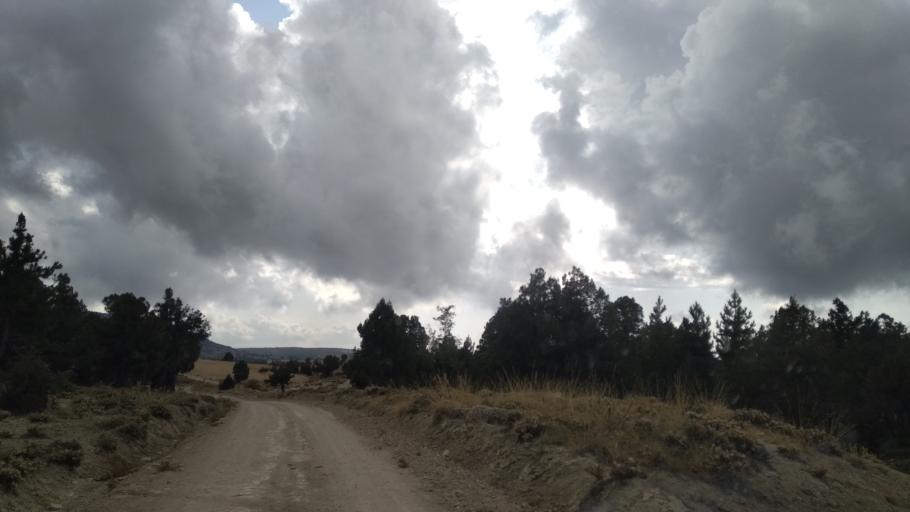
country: TR
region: Mersin
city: Sarikavak
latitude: 36.5734
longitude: 33.7528
